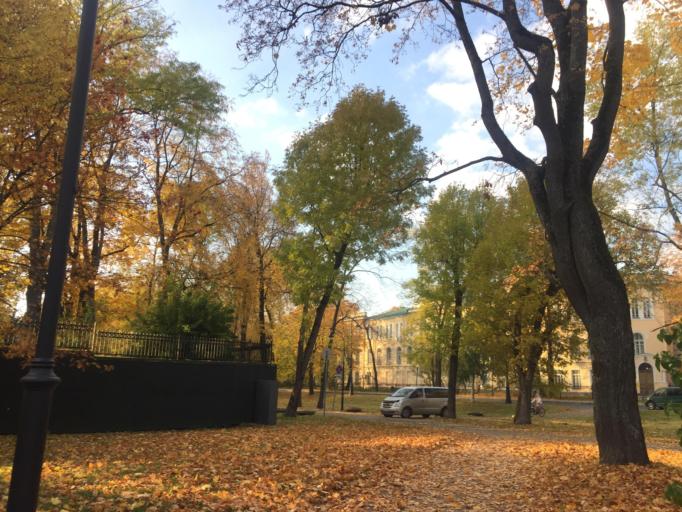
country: RU
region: Leningrad
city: Chernaya Rechka
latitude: 59.9795
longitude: 30.2962
